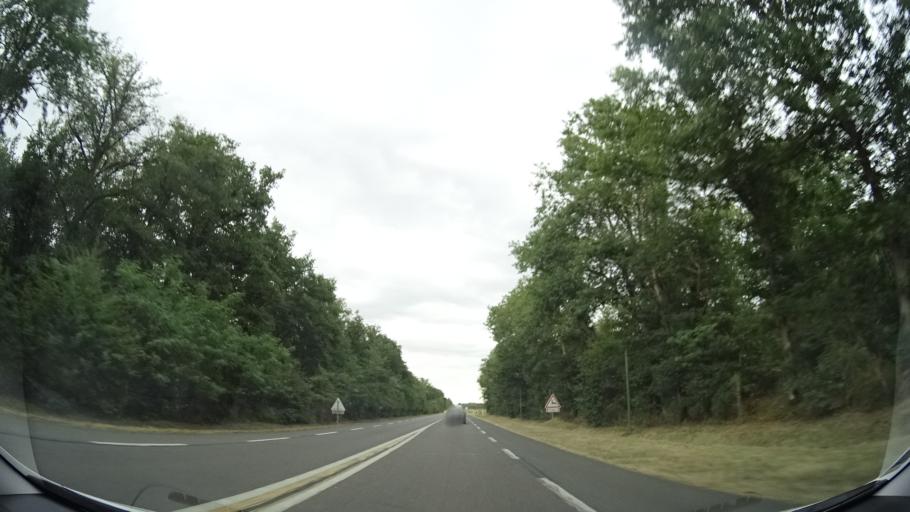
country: FR
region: Centre
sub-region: Departement du Loiret
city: Vitry-aux-Loges
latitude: 47.8919
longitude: 2.2694
